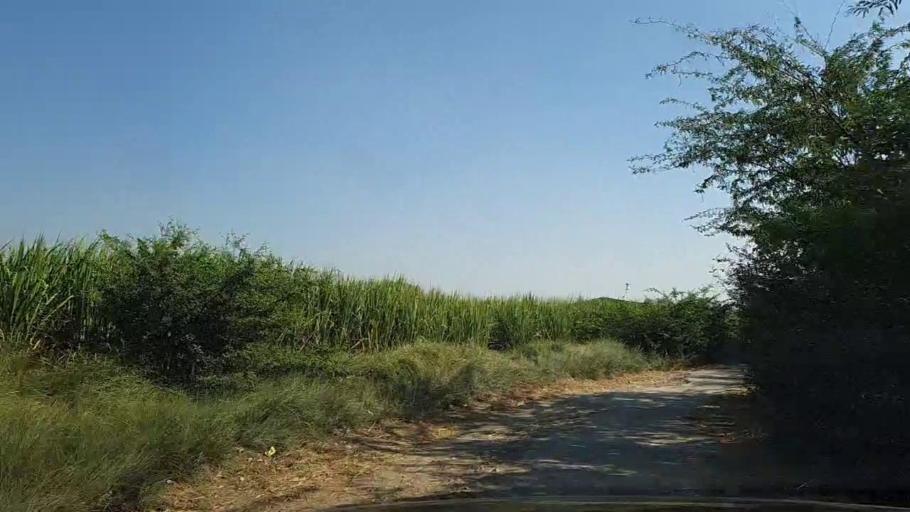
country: PK
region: Sindh
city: Daro Mehar
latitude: 24.7710
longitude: 68.0690
